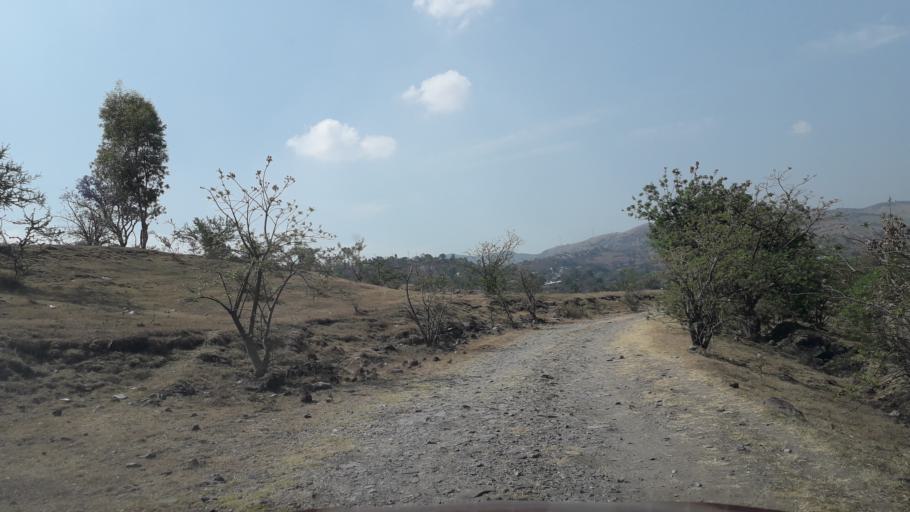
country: MX
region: Puebla
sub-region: Puebla
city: San Andres Azumiatla
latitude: 18.9128
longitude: -98.2590
